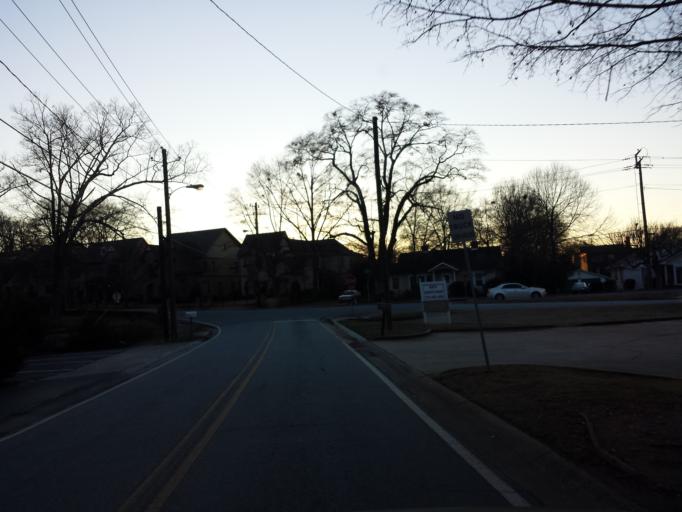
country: US
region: Georgia
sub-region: Cobb County
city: Smyrna
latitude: 33.8882
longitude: -84.5113
